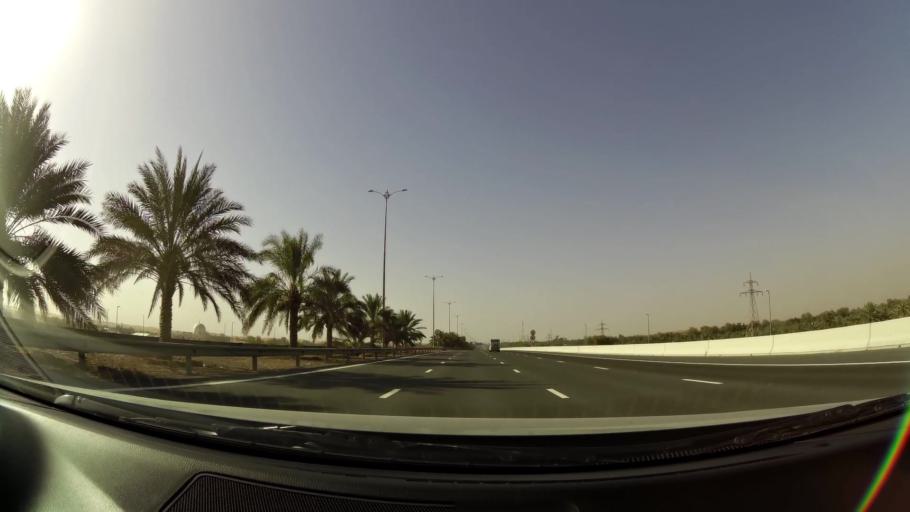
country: OM
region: Al Buraimi
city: Al Buraymi
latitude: 24.4293
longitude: 55.7883
